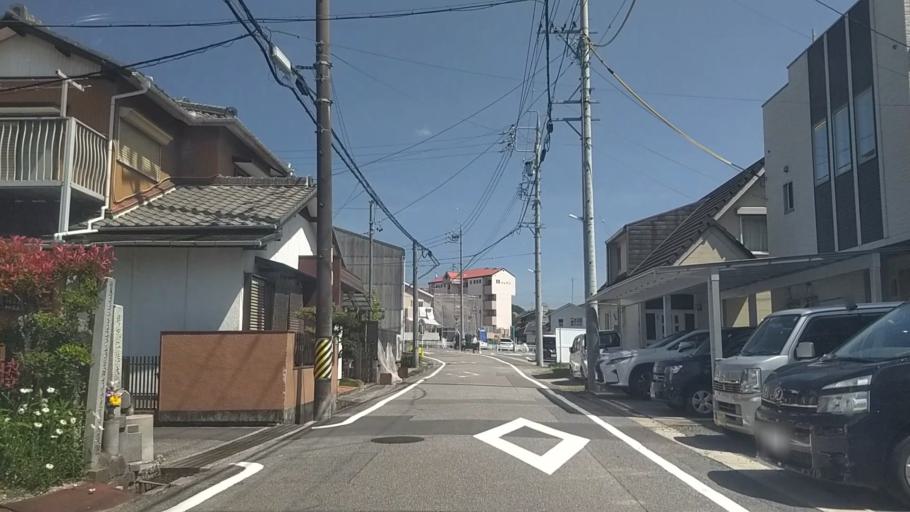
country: JP
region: Aichi
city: Okazaki
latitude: 34.9766
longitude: 137.1768
